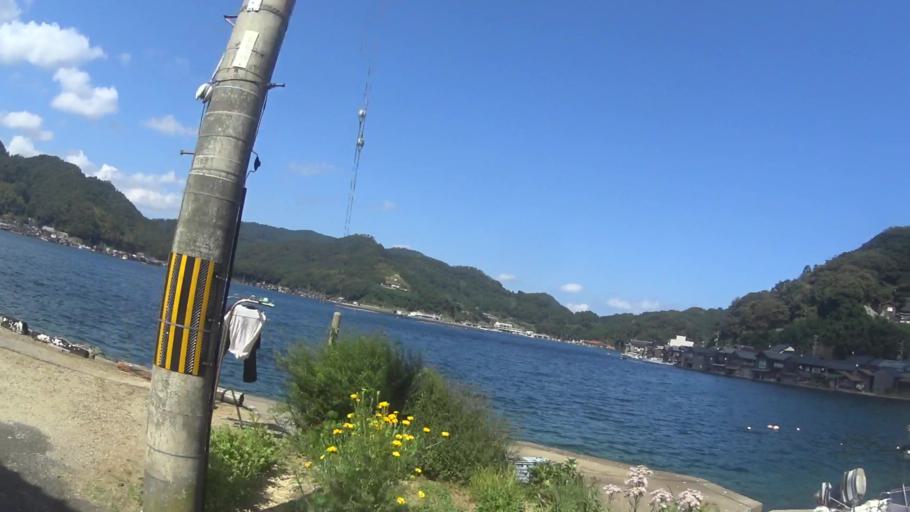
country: JP
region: Kyoto
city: Miyazu
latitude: 35.6662
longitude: 135.2895
